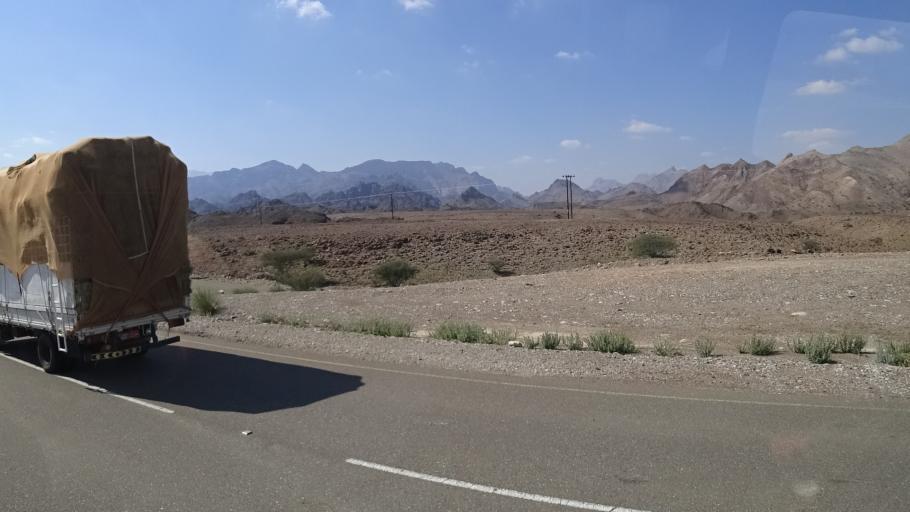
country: OM
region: Al Batinah
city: Al Khaburah
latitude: 23.7529
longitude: 56.9237
